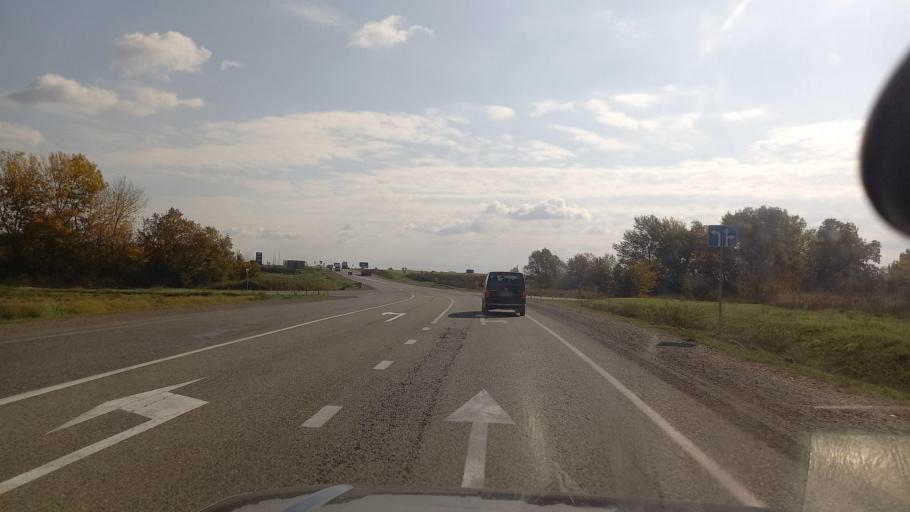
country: RU
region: Krasnodarskiy
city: Abinsk
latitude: 44.8750
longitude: 38.1107
